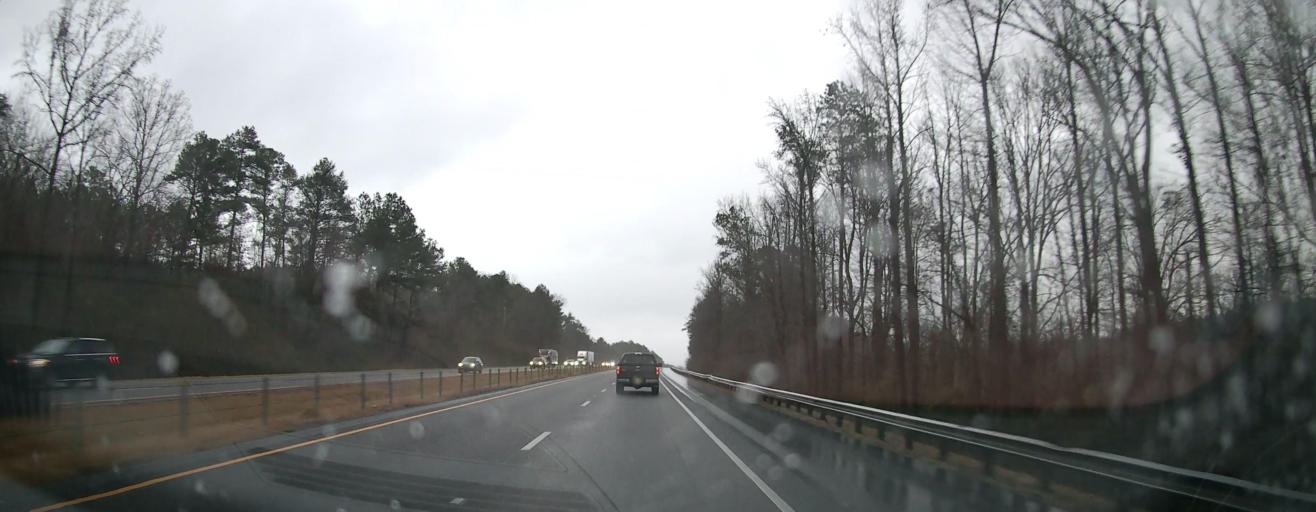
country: US
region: Alabama
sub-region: Cullman County
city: Good Hope
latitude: 34.0101
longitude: -86.8641
